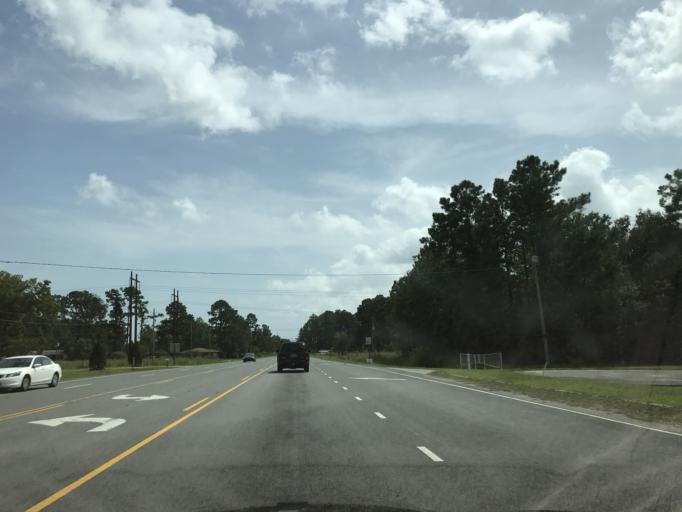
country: US
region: North Carolina
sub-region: New Hanover County
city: Wrightsboro
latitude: 34.3130
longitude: -77.9222
